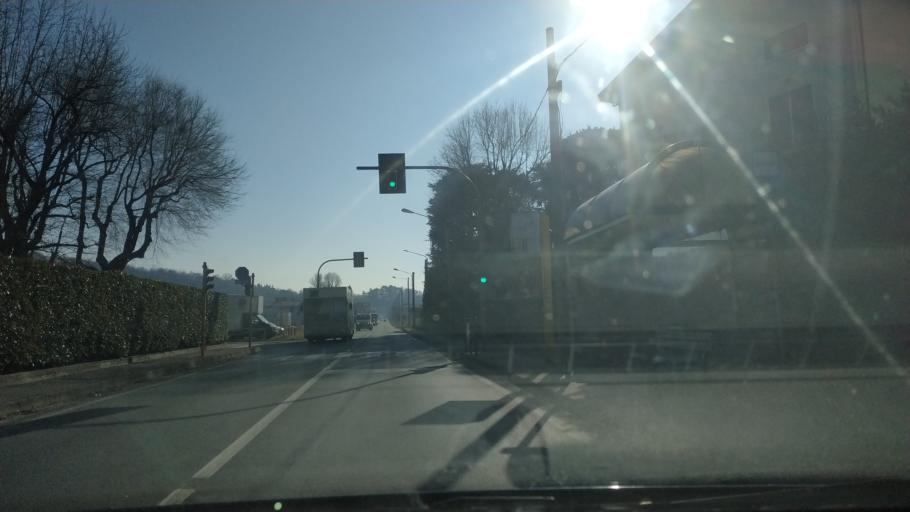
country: IT
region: Piedmont
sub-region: Provincia di Torino
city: Montalto Dora
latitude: 45.4824
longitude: 7.8634
